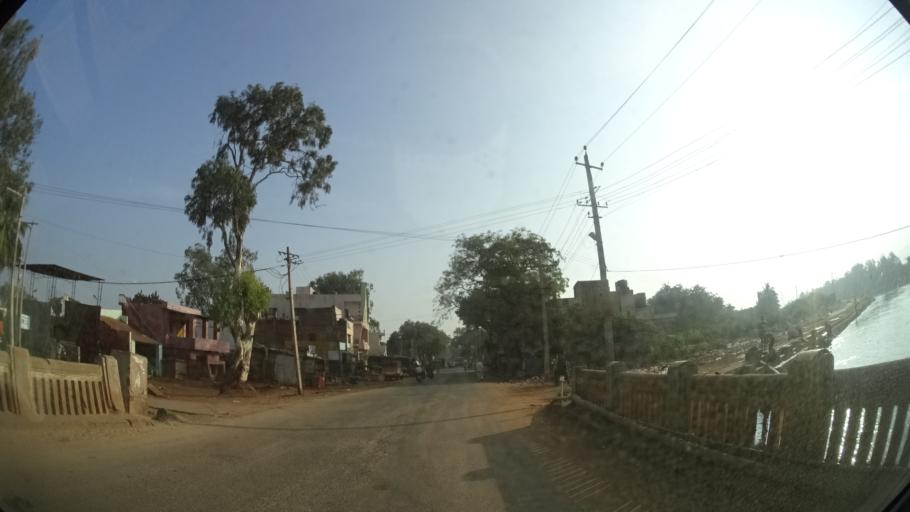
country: IN
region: Karnataka
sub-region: Bellary
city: Hospet
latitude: 15.2602
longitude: 76.3809
